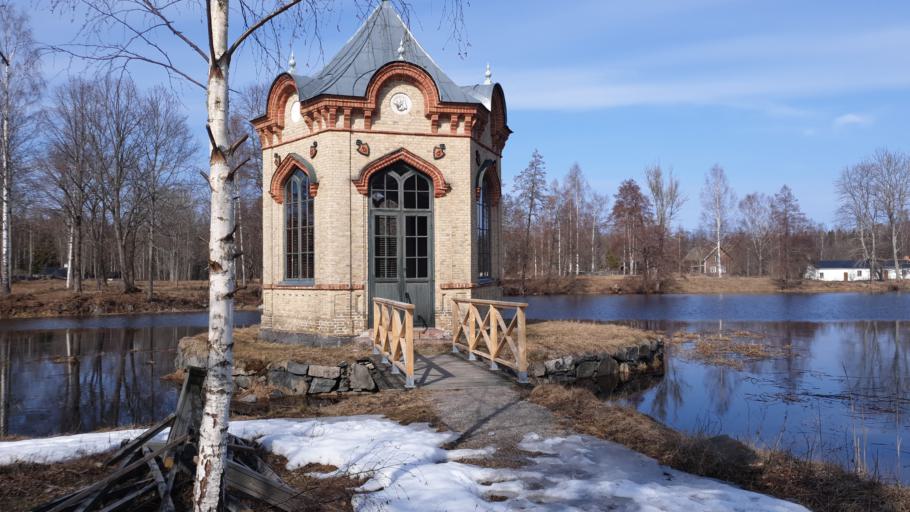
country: SE
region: Gaevleborg
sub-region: Gavle Kommun
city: Norrsundet
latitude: 61.0461
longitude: 17.1407
